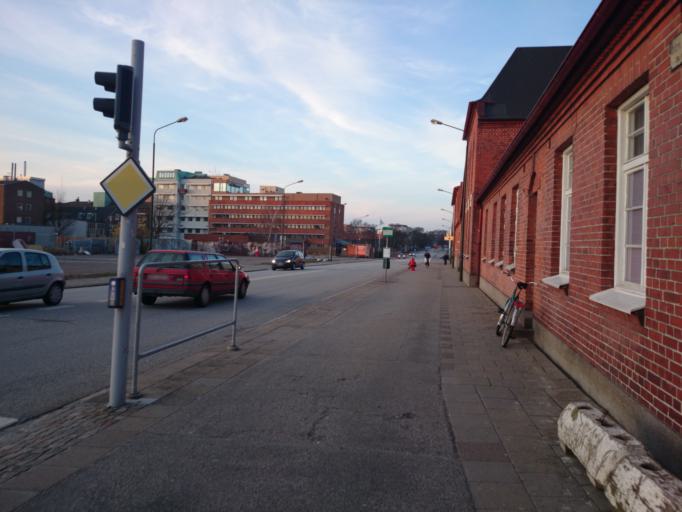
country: SE
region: Skane
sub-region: Malmo
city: Malmoe
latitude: 55.5983
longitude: 13.0303
